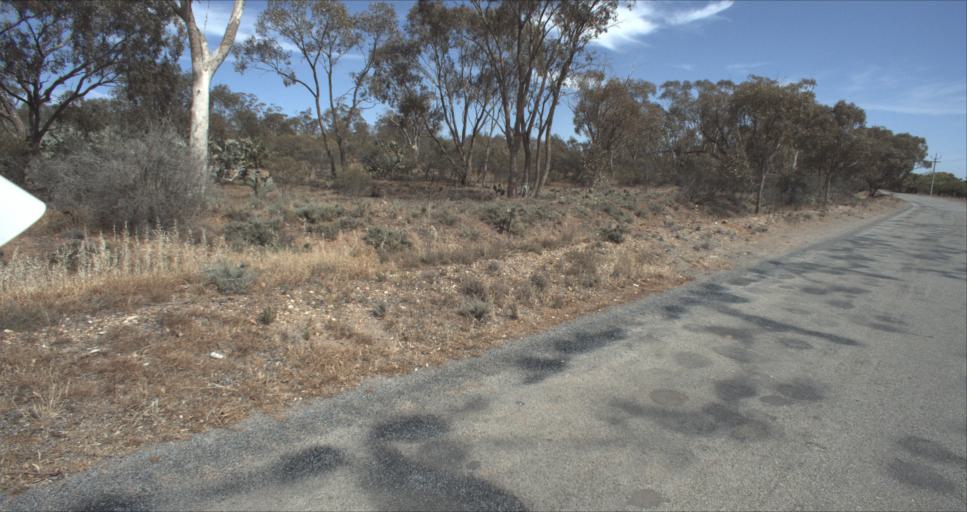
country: AU
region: New South Wales
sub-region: Leeton
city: Leeton
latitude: -34.5637
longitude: 146.4616
